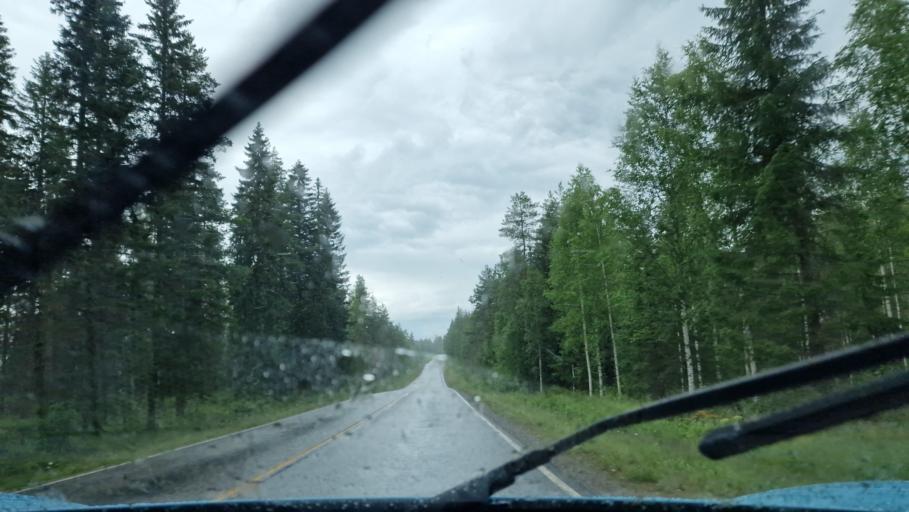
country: FI
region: Central Finland
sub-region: Saarijaervi-Viitasaari
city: Pylkoenmaeki
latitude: 62.5942
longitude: 24.5901
